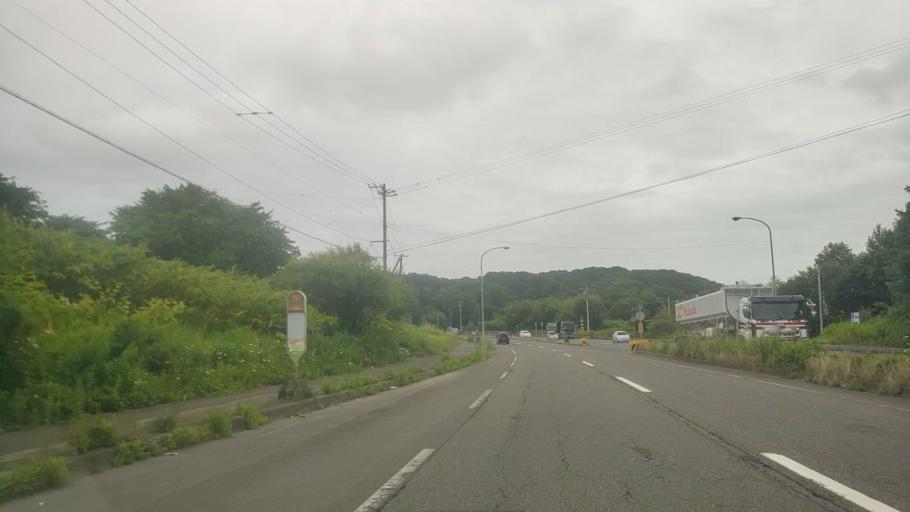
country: JP
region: Hokkaido
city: Shiraoi
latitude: 42.4566
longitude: 141.1878
